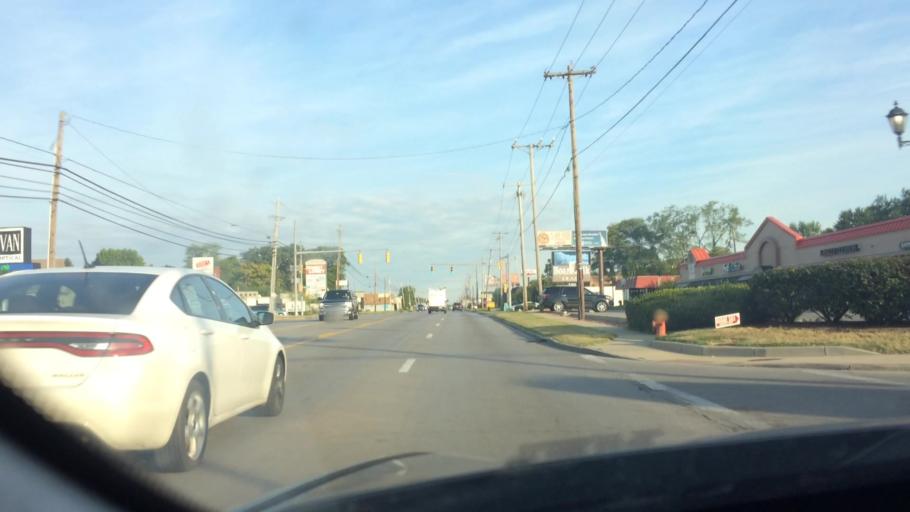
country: US
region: Ohio
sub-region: Lucas County
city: Ottawa Hills
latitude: 41.7029
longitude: -83.6554
